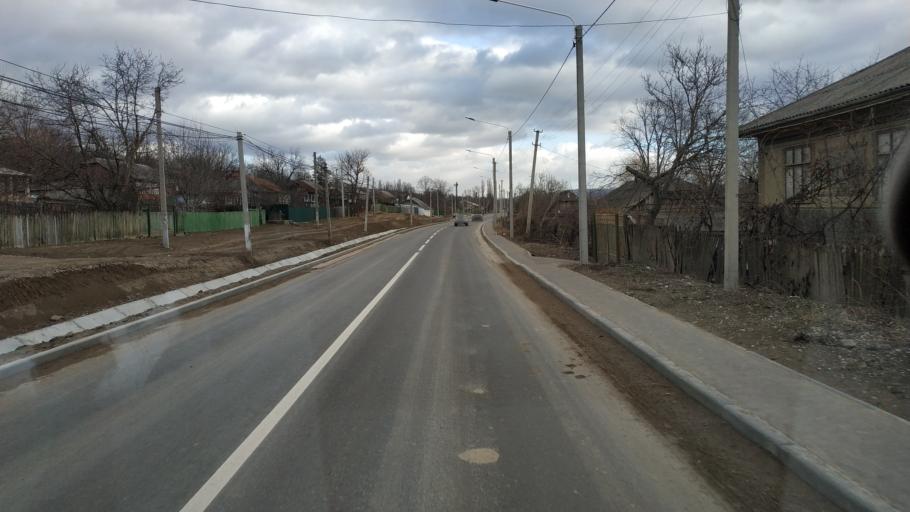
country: MD
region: Calarasi
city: Calarasi
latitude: 47.2836
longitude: 28.2031
